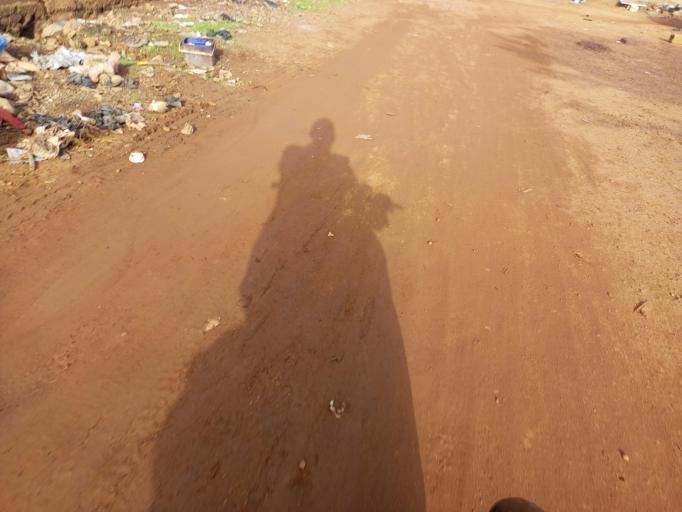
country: ML
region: Bamako
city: Bamako
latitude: 12.5205
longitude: -7.9922
